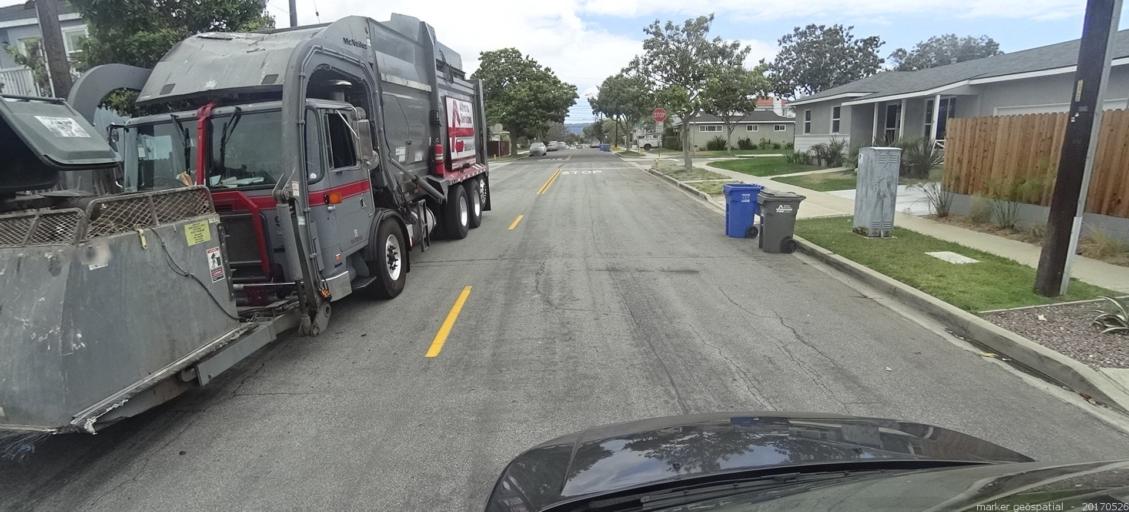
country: US
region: California
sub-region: Los Angeles County
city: Lawndale
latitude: 33.8610
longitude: -118.3578
